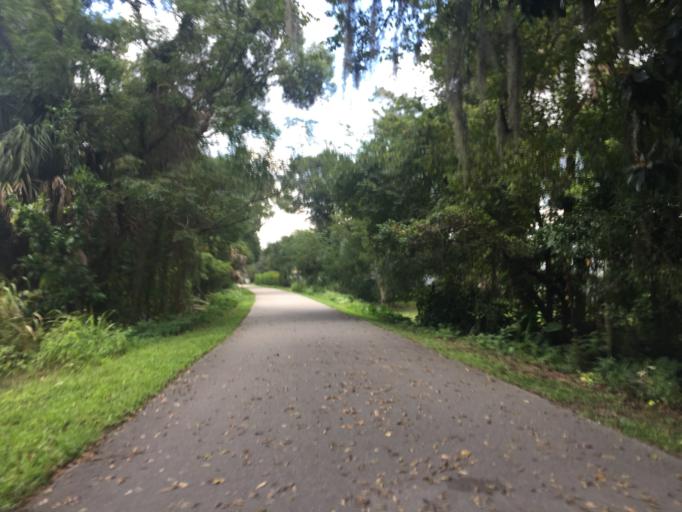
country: US
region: Florida
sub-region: Seminole County
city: Oviedo
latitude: 28.6750
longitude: -81.2116
